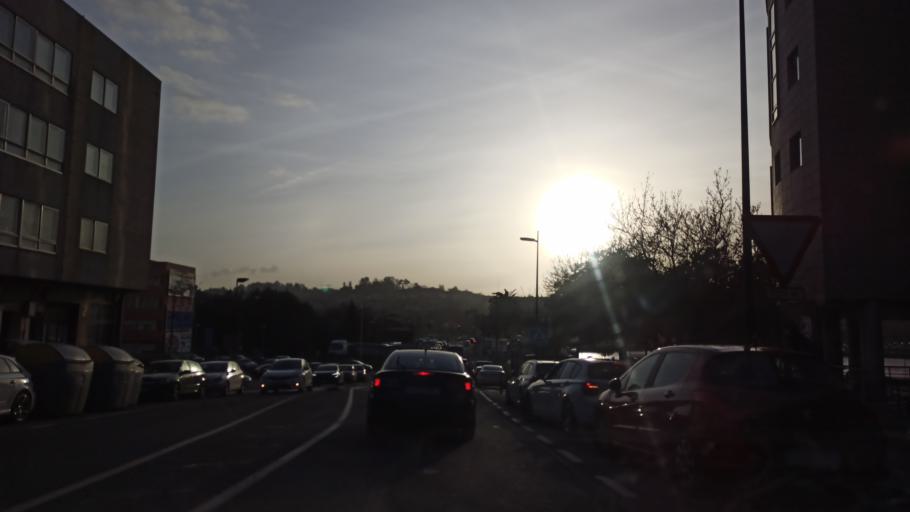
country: ES
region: Galicia
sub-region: Provincia da Coruna
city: Cambre
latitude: 43.3174
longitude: -8.3572
